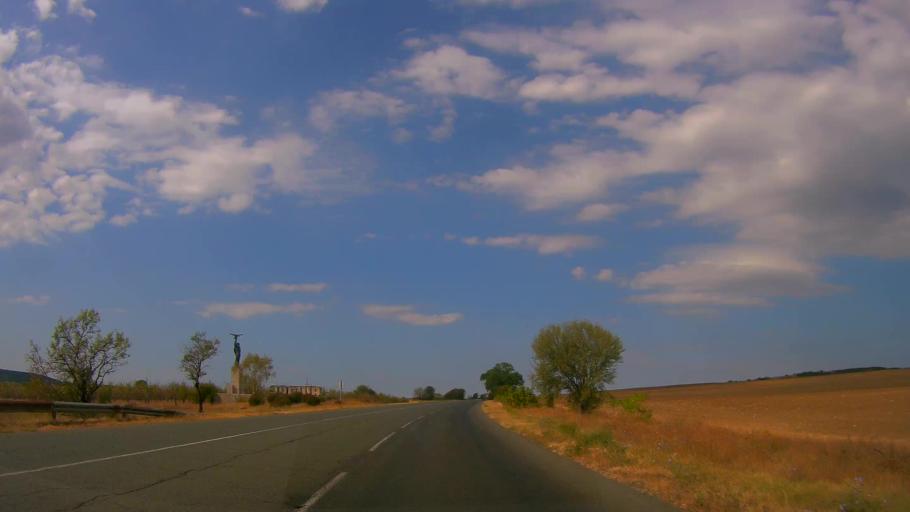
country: BG
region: Burgas
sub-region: Obshtina Aytos
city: Aytos
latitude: 42.6972
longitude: 27.2005
